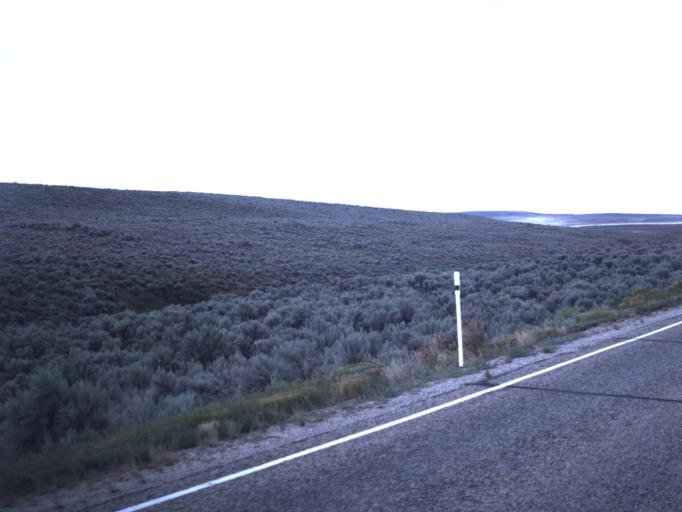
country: US
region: Utah
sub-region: Rich County
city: Randolph
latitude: 41.7913
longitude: -111.2163
